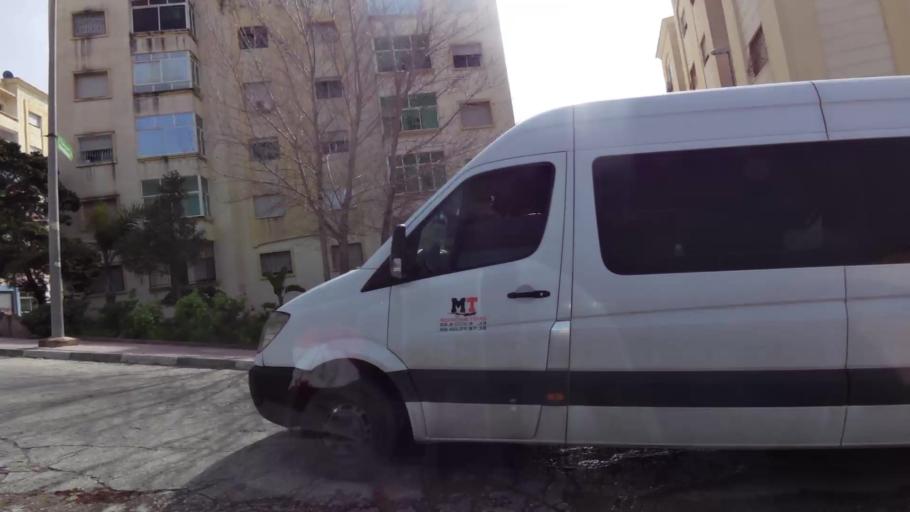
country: MA
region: Tanger-Tetouan
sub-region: Tanger-Assilah
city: Boukhalef
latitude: 35.7413
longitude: -5.8675
